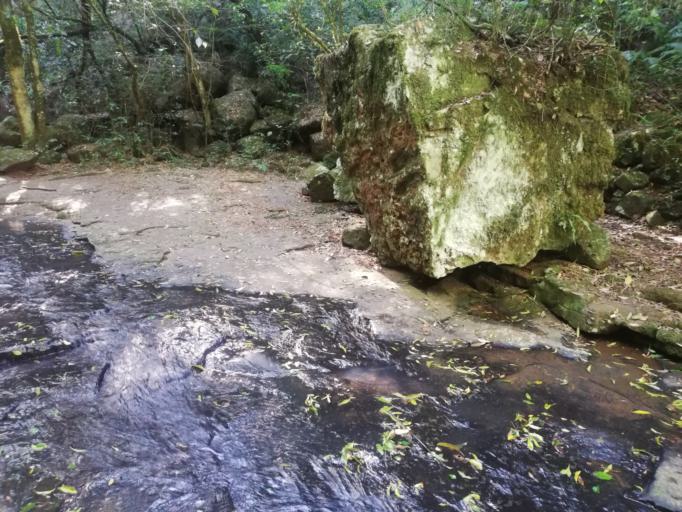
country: AR
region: Misiones
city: Cerro Azul
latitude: -27.7534
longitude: -55.5628
